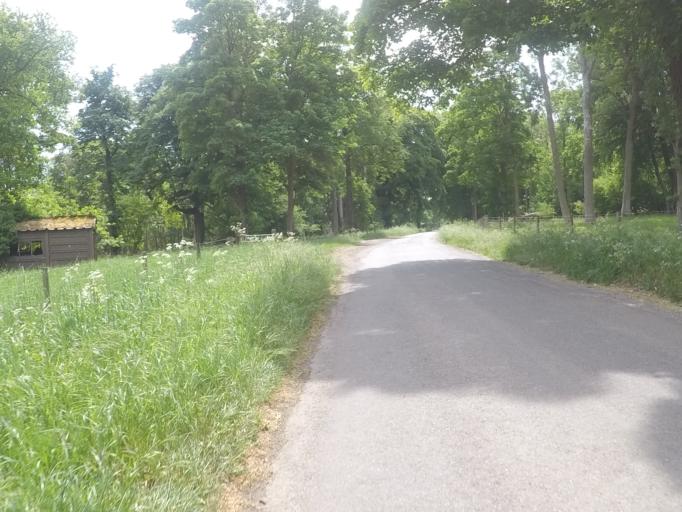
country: GB
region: England
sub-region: Oxfordshire
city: Charlbury
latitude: 51.8679
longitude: -1.5148
